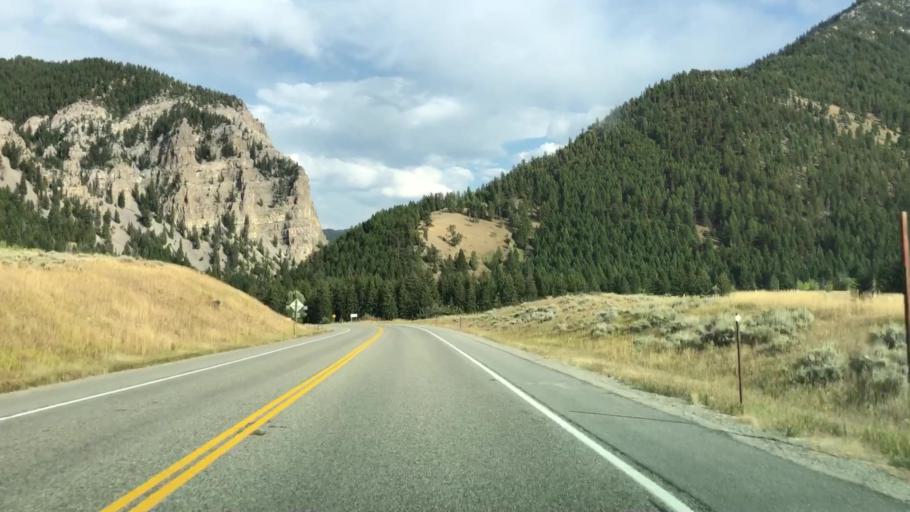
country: US
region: Wyoming
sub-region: Teton County
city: Hoback
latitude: 43.2891
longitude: -110.6414
